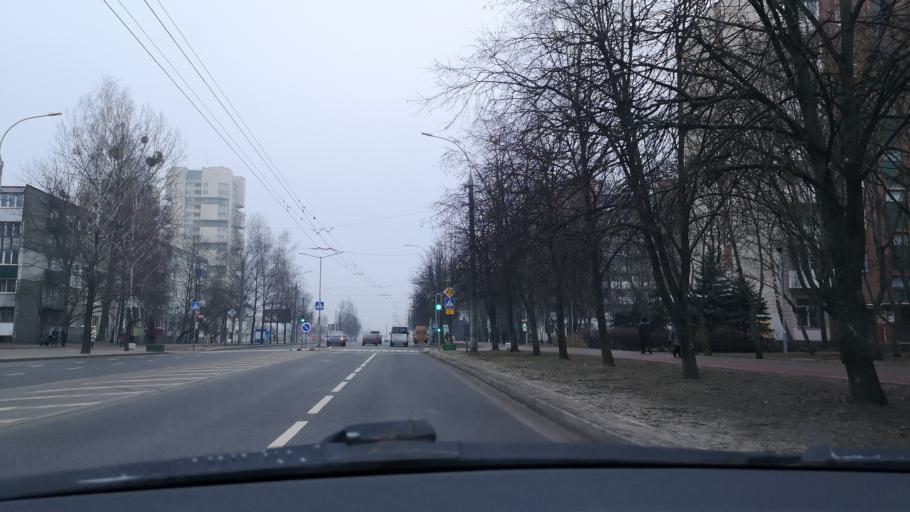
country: BY
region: Brest
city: Brest
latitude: 52.1028
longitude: 23.7622
